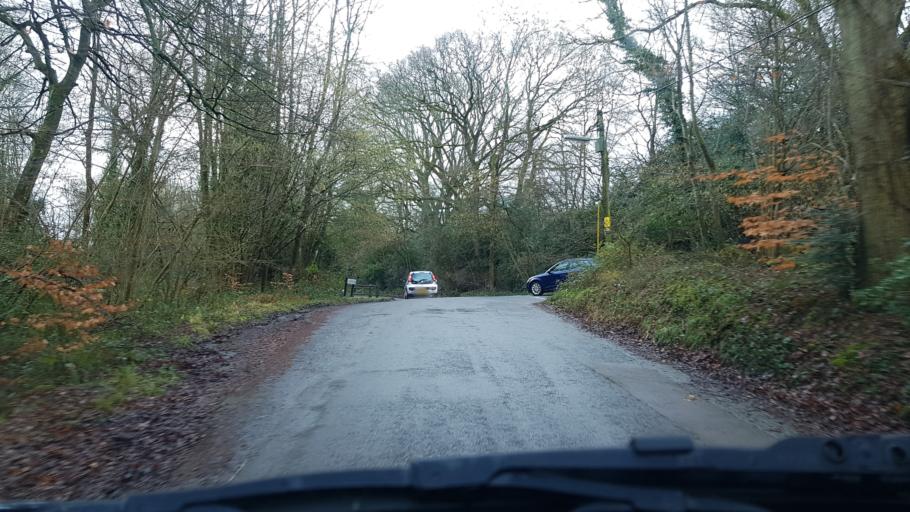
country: GB
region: England
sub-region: Surrey
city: Haslemere
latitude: 51.1005
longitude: -0.6877
